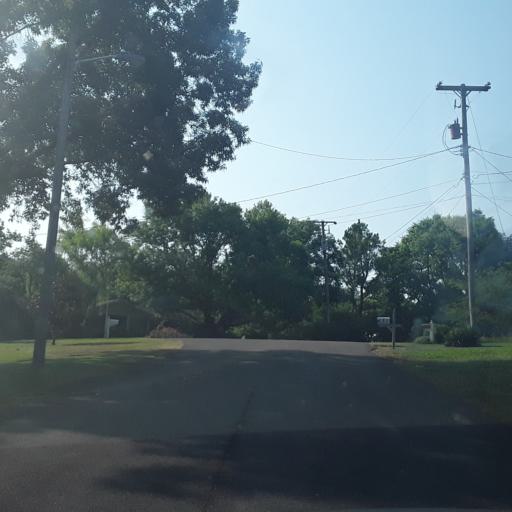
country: US
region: Tennessee
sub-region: Williamson County
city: Brentwood Estates
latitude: 36.0292
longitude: -86.7156
